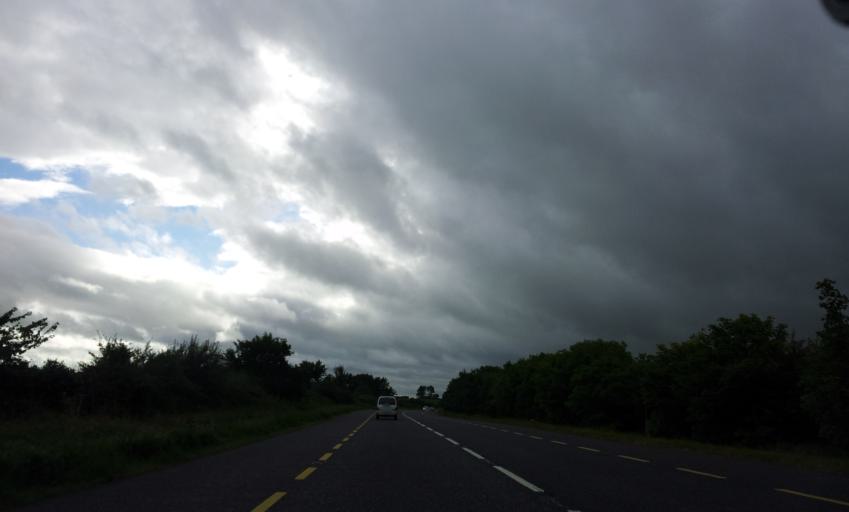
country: IE
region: Munster
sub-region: County Cork
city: Youghal
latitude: 51.9389
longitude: -7.9353
